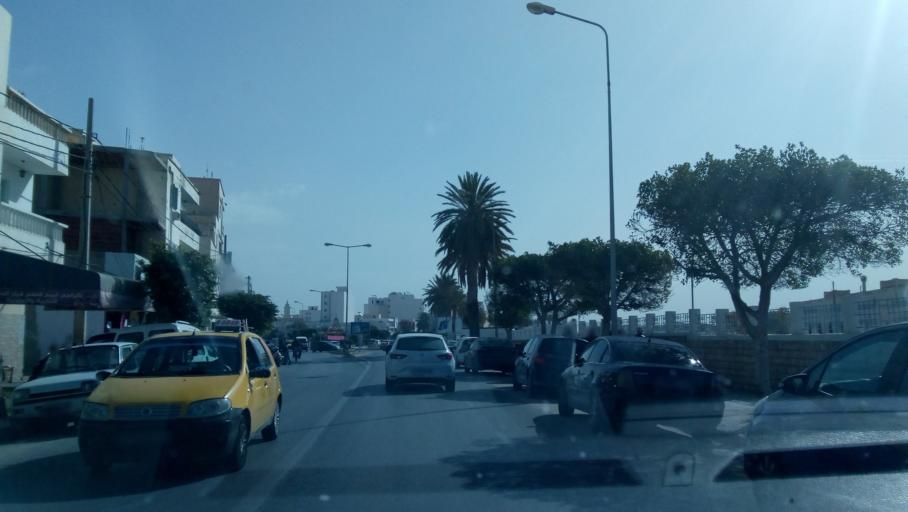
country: TN
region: Qabis
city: Gabes
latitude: 33.8850
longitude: 10.0946
